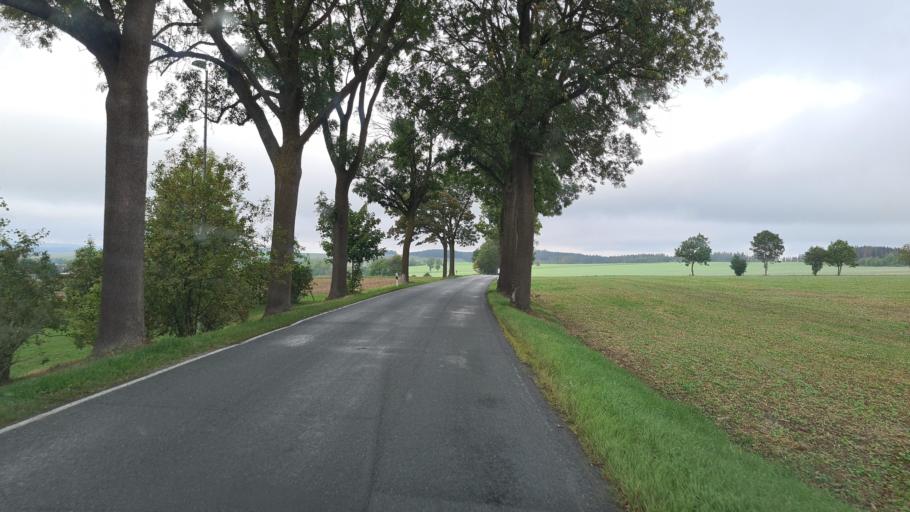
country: DE
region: Thuringia
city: Wurzbach
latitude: 50.5254
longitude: 11.5364
